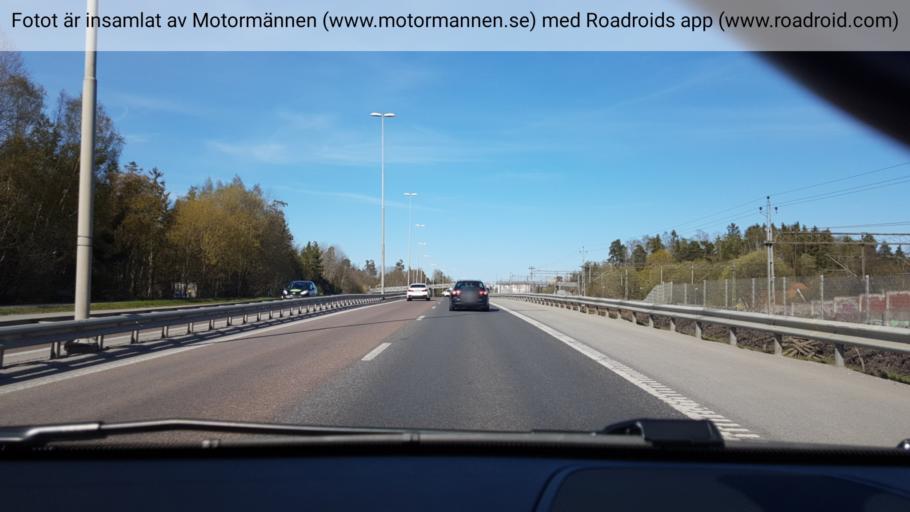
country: SE
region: Stockholm
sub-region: Huddinge Kommun
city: Huddinge
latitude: 59.2294
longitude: 17.9646
